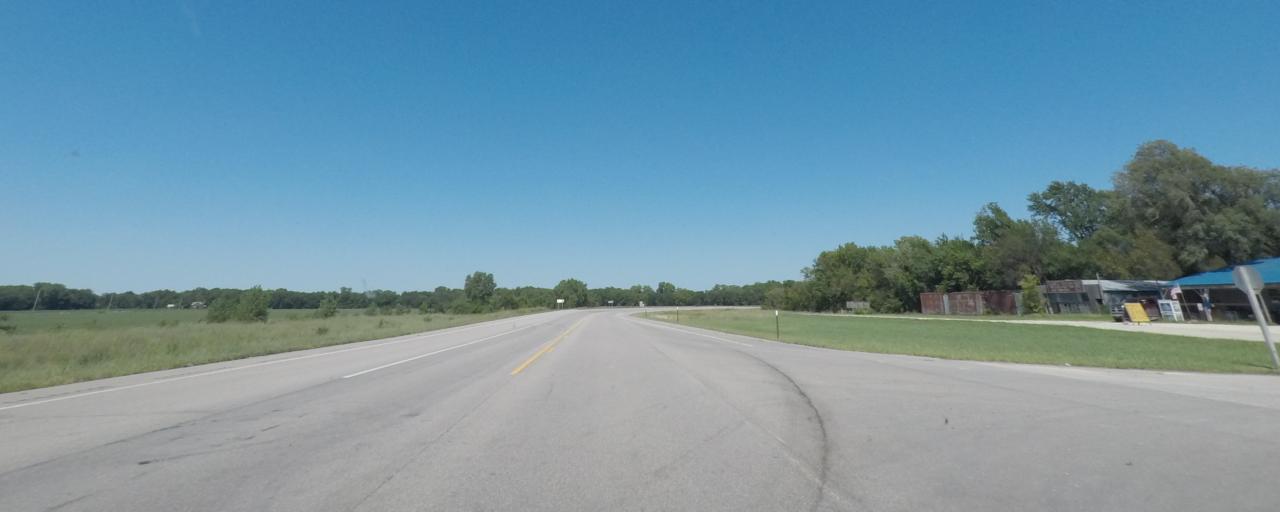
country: US
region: Kansas
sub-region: Chase County
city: Cottonwood Falls
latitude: 38.3735
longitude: -96.6501
